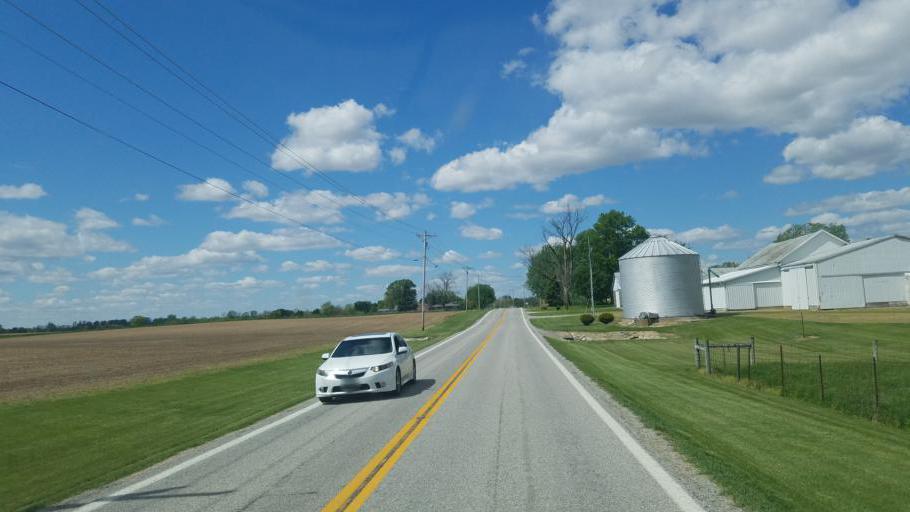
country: US
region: Ohio
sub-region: Marion County
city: Prospect
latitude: 40.3782
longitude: -83.1903
